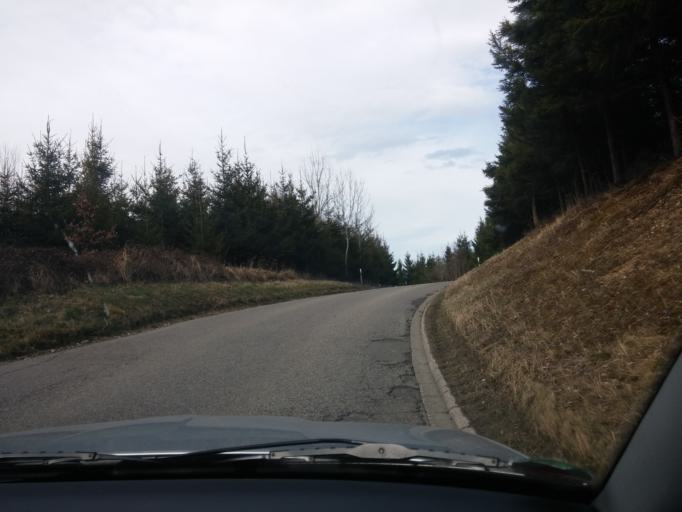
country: DE
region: Bavaria
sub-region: Swabia
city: Woringen
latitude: 47.9195
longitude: 10.1866
